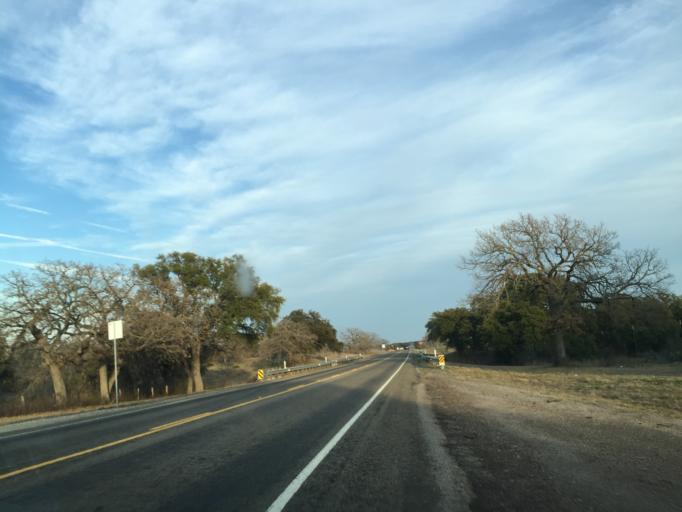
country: US
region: Texas
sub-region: Llano County
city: Buchanan Dam
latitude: 30.7327
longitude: -98.4958
